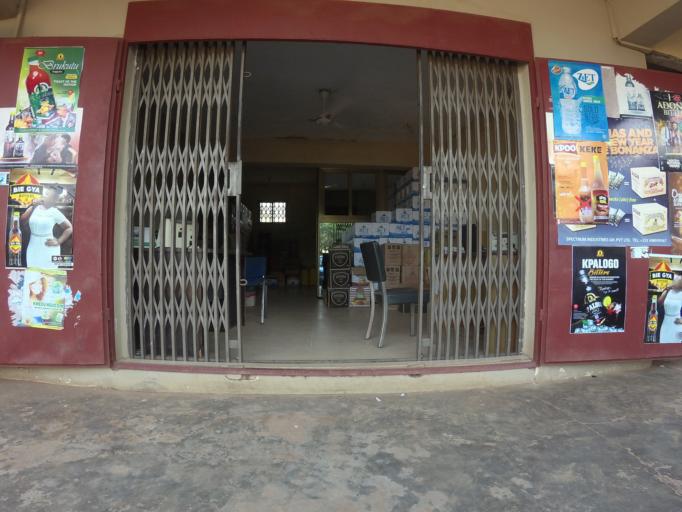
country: GH
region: Greater Accra
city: Nungua
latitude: 5.6306
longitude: -0.0953
